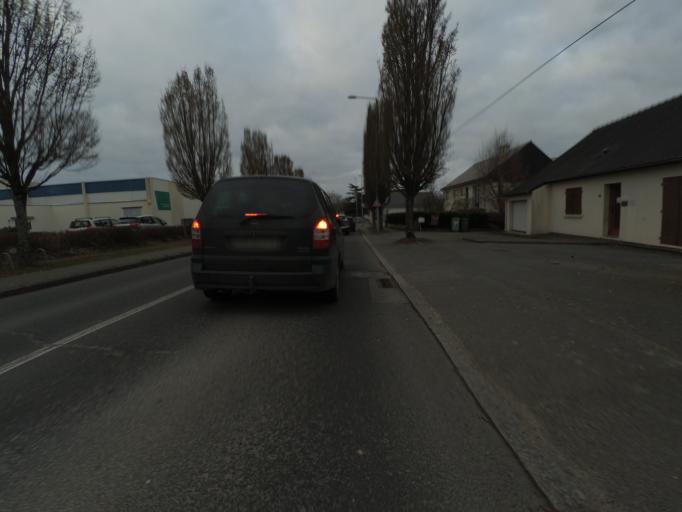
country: FR
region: Pays de la Loire
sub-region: Departement de la Loire-Atlantique
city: Carquefou
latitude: 47.2955
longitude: -1.4868
